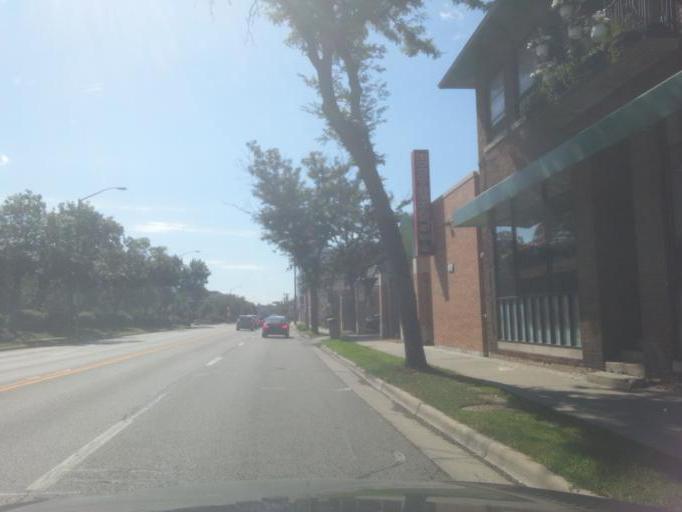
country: US
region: Wisconsin
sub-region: Dane County
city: Madison
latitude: 43.0677
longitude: -89.3992
